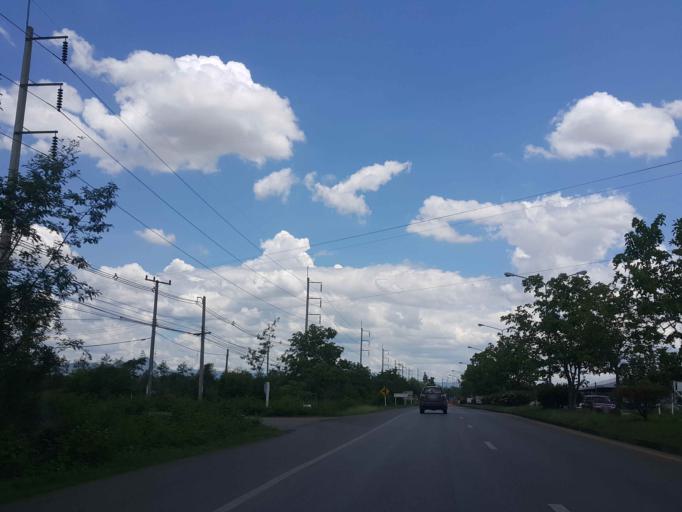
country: TH
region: Phrae
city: Nong Muang Khai
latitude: 18.2137
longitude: 100.1988
